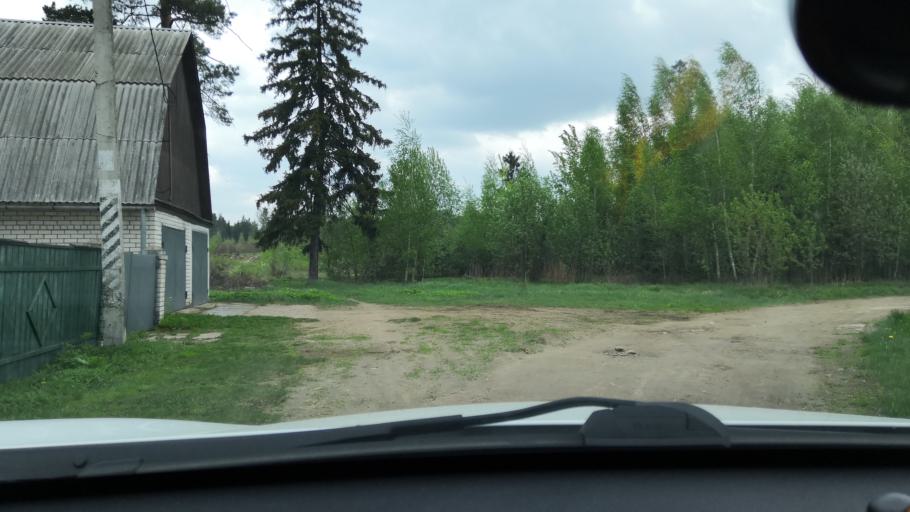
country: RU
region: Moskovskaya
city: Povarovo
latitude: 56.0820
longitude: 37.0616
